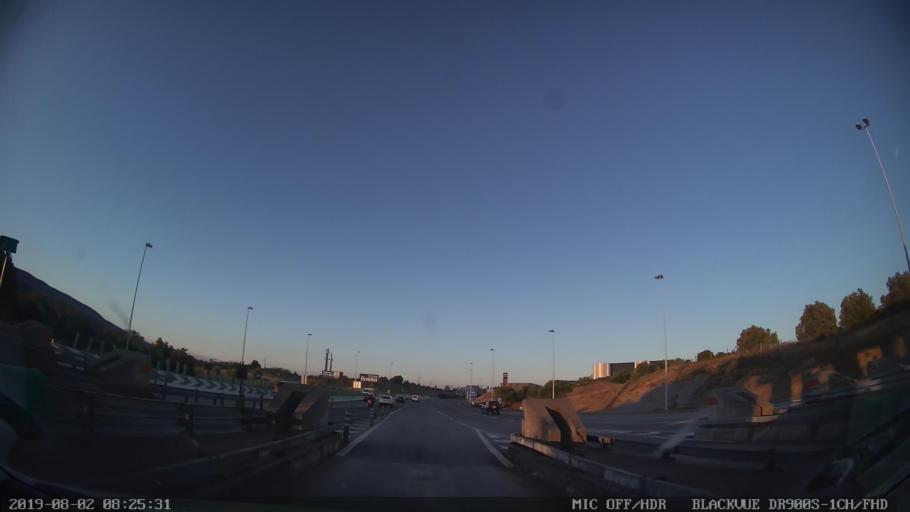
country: PT
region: Santarem
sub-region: Alcanena
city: Alcanena
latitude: 39.4783
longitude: -8.6270
